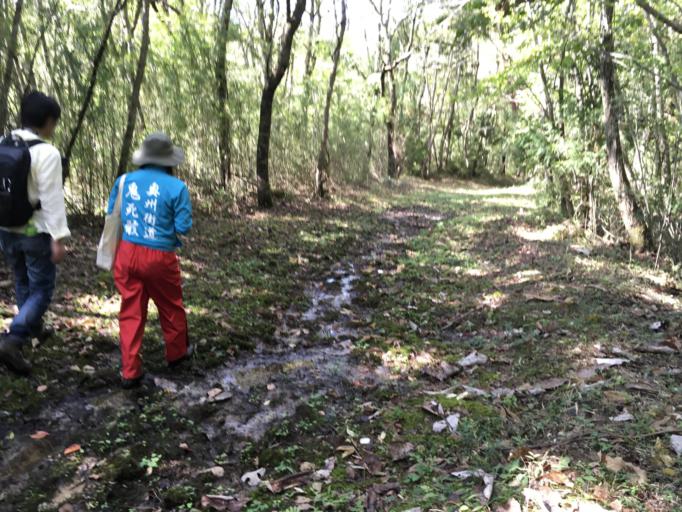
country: JP
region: Iwate
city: Ichinoseki
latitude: 38.8750
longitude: 141.1246
